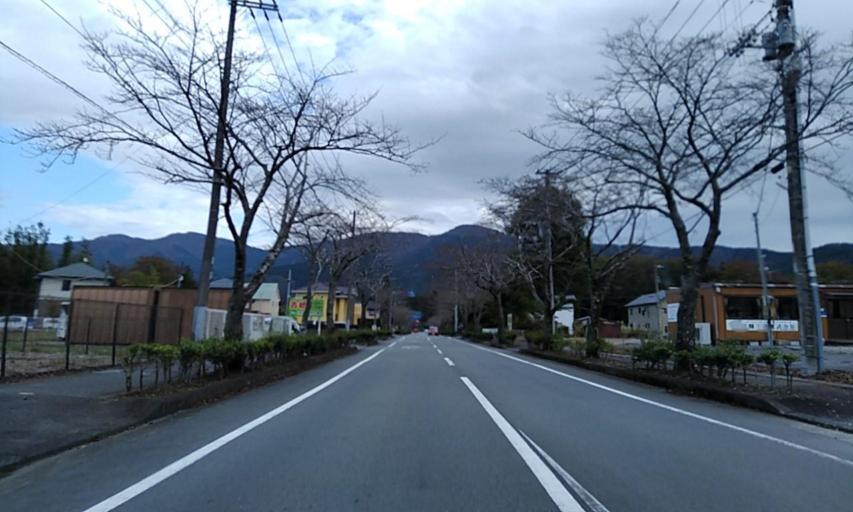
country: JP
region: Shizuoka
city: Gotemba
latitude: 35.2901
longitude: 138.9410
